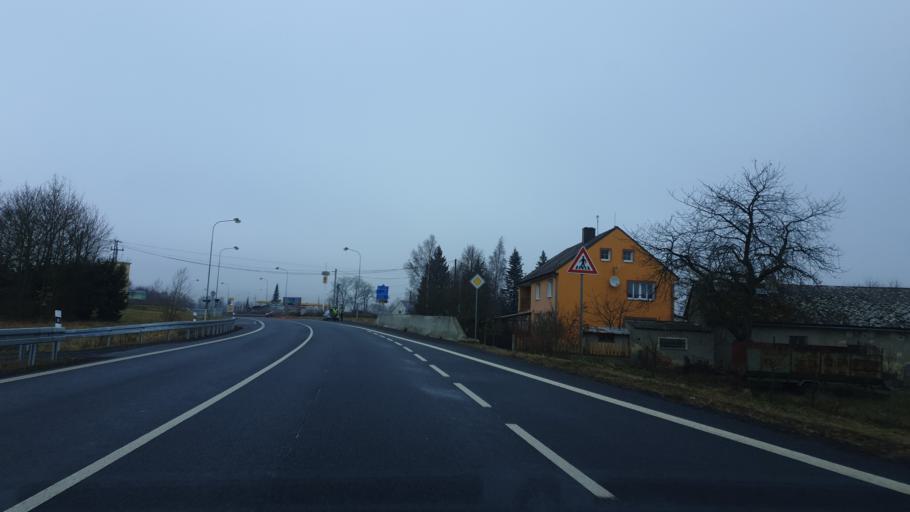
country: CZ
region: Karlovarsky
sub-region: Okres Cheb
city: Skalna
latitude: 50.1647
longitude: 12.3180
